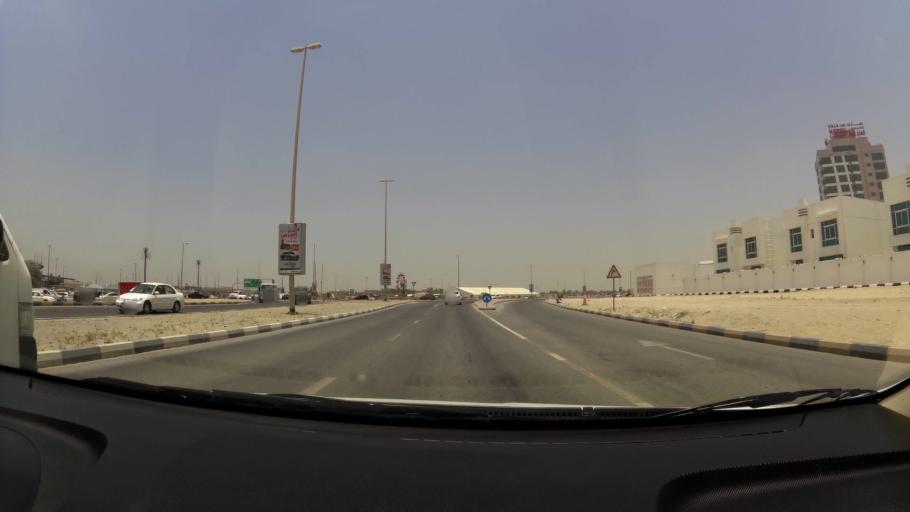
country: AE
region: Ajman
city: Ajman
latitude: 25.4008
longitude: 55.4818
